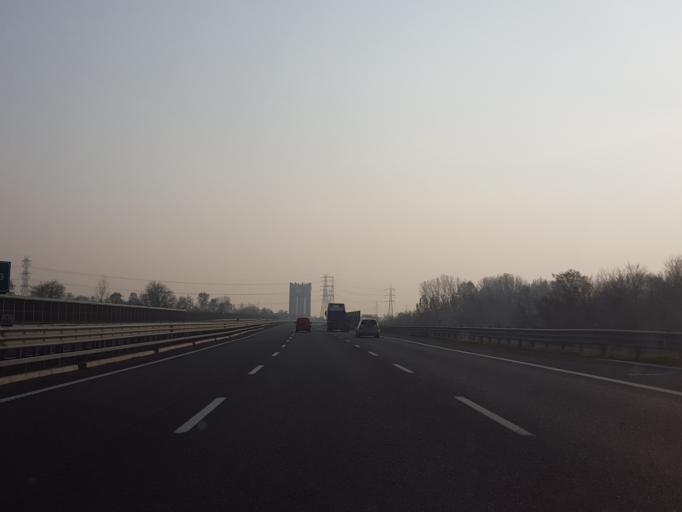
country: IT
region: Veneto
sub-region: Provincia di Venezia
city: Maerne
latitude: 45.5111
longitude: 12.1394
